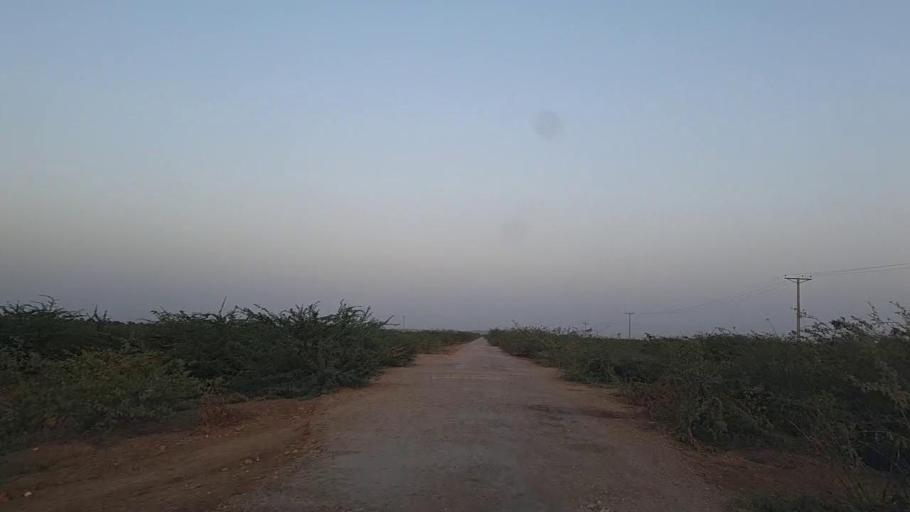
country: PK
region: Sindh
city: Naukot
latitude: 24.7200
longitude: 69.2928
